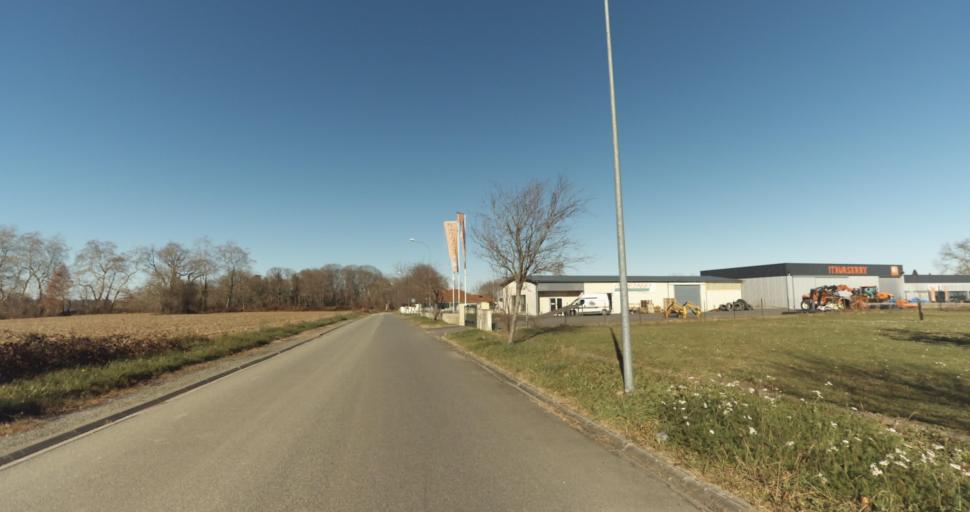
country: FR
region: Aquitaine
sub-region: Departement des Pyrenees-Atlantiques
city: Morlaas
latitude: 43.3527
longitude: -0.2583
